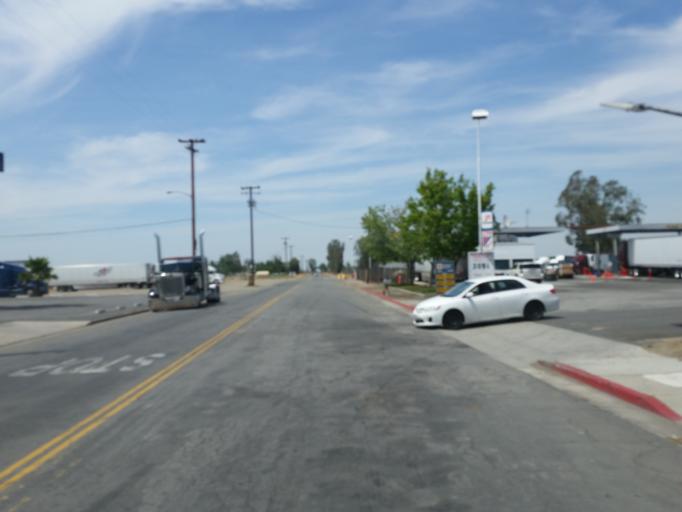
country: US
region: California
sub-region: Kern County
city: Greenfield
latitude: 35.2103
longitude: -119.0120
